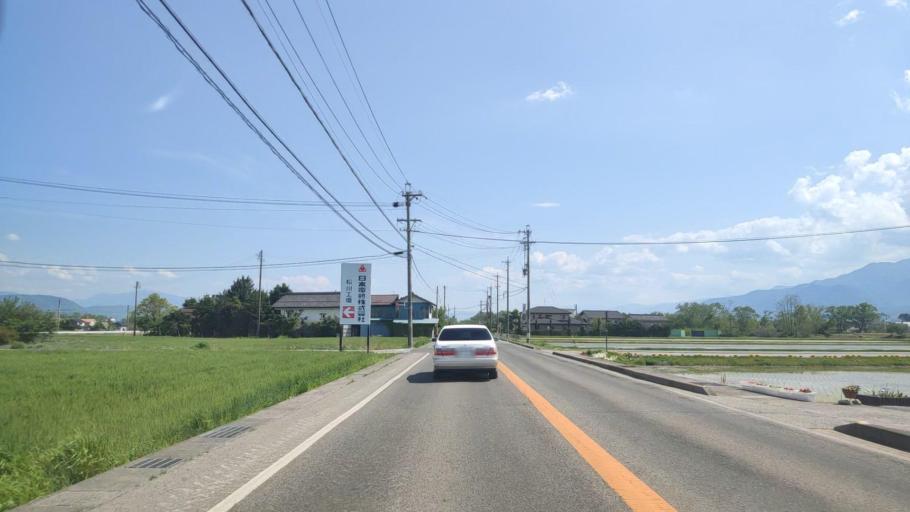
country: JP
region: Nagano
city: Hotaka
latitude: 36.3891
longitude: 137.8646
